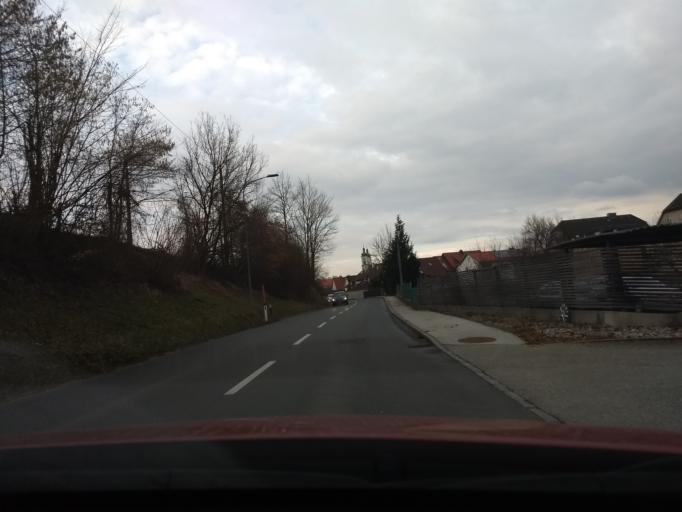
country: AT
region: Upper Austria
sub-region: Politischer Bezirk Steyr-Land
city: Garsten
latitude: 48.0154
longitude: 14.4064
